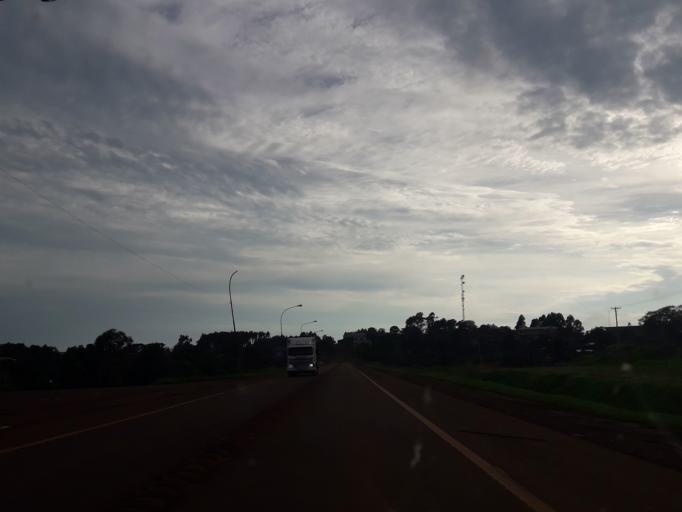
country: AR
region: Misiones
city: Dos de Mayo
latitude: -26.9900
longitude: -54.4832
